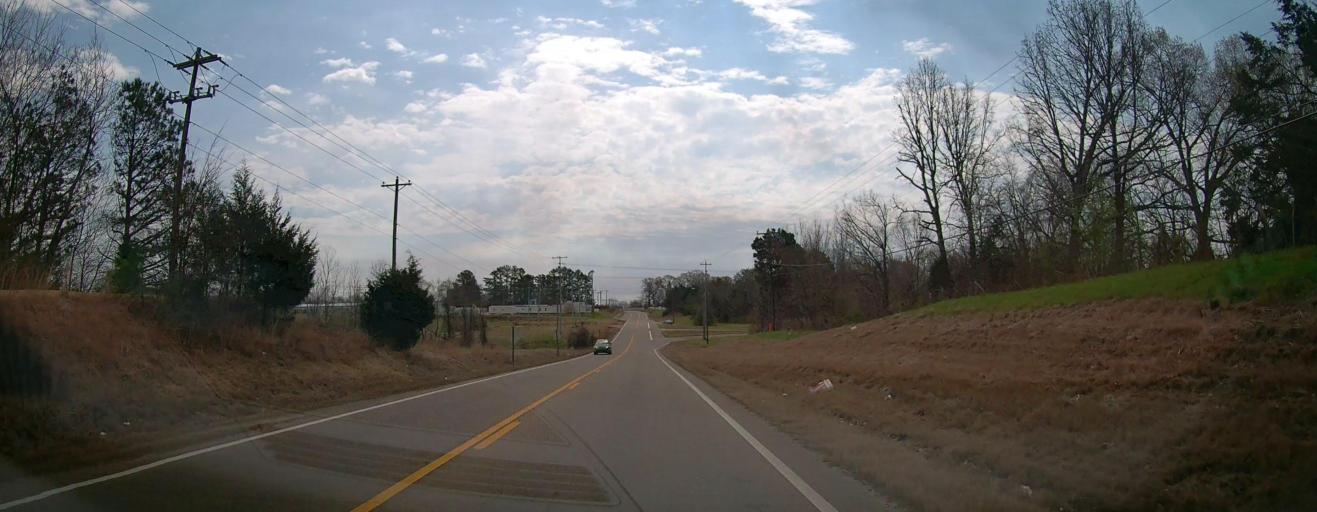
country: US
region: Mississippi
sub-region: De Soto County
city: Olive Branch
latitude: 34.9846
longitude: -89.8599
